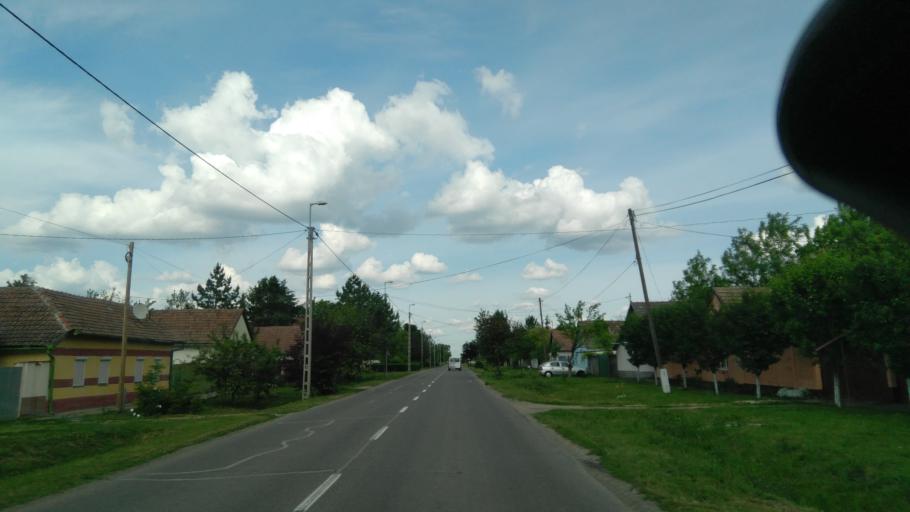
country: HU
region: Bekes
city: Battonya
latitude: 46.2926
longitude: 21.0263
